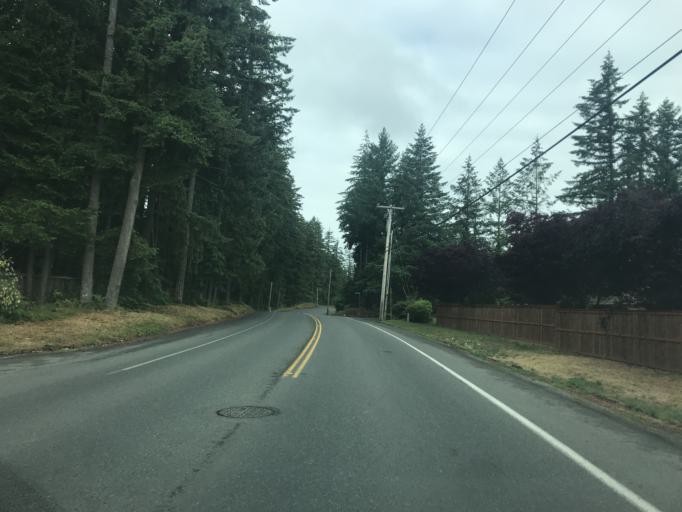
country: US
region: Washington
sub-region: King County
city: Lake Morton-Berrydale
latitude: 47.3418
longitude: -122.0593
